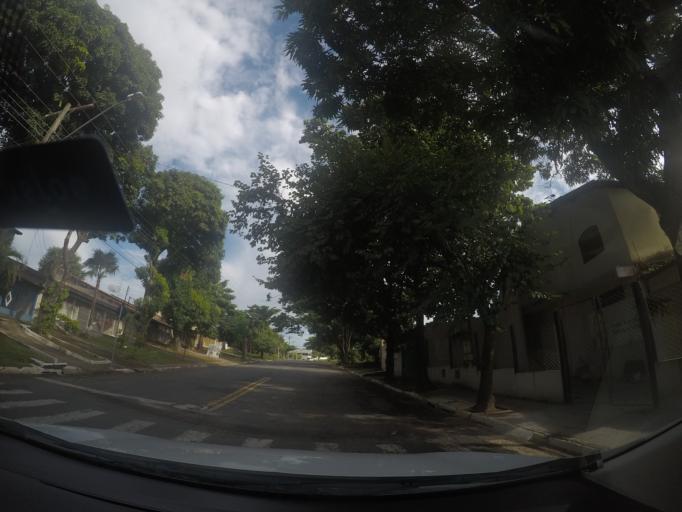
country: BR
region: Goias
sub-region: Goiania
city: Goiania
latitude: -16.6943
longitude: -49.2028
